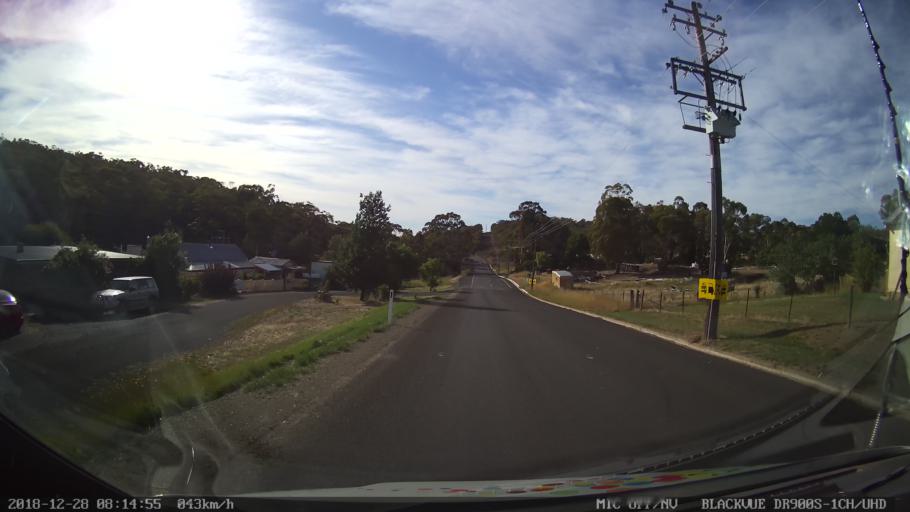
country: AU
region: New South Wales
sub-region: Blayney
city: Blayney
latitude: -33.8203
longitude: 149.3253
